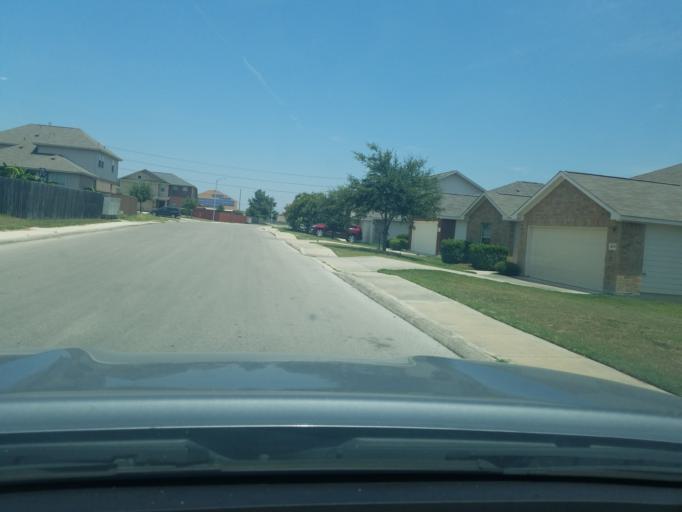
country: US
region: Texas
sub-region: Bexar County
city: Kirby
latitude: 29.4654
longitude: -98.3316
